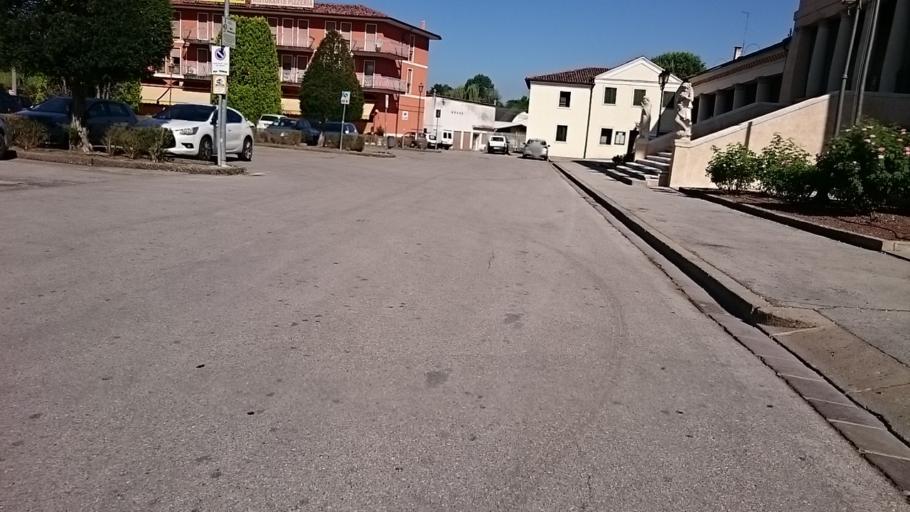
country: IT
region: Veneto
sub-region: Provincia di Vicenza
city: Montegalda
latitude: 45.4437
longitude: 11.6726
